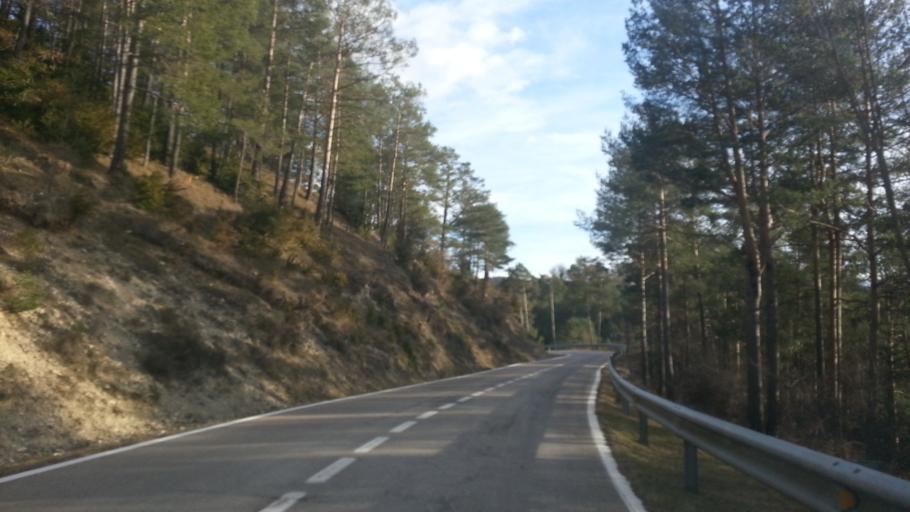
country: ES
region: Catalonia
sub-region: Provincia de Girona
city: Toses
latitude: 42.2449
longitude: 2.0160
